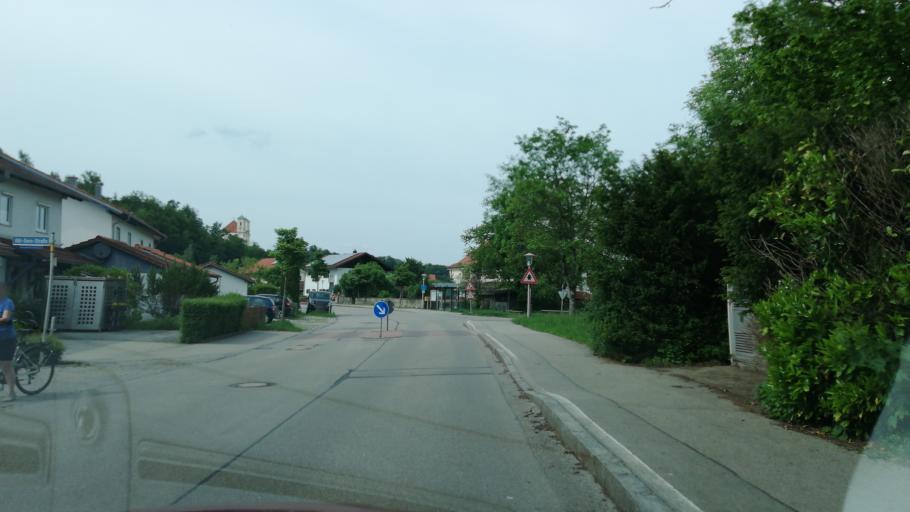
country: DE
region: Bavaria
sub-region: Upper Bavaria
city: Mehring
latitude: 48.1359
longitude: 12.7905
